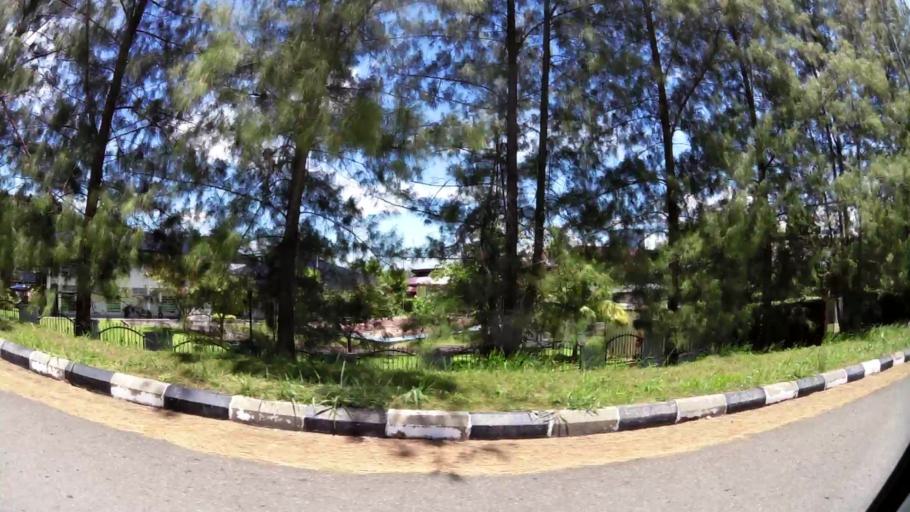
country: BN
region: Brunei and Muara
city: Bandar Seri Begawan
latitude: 4.9230
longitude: 114.9593
